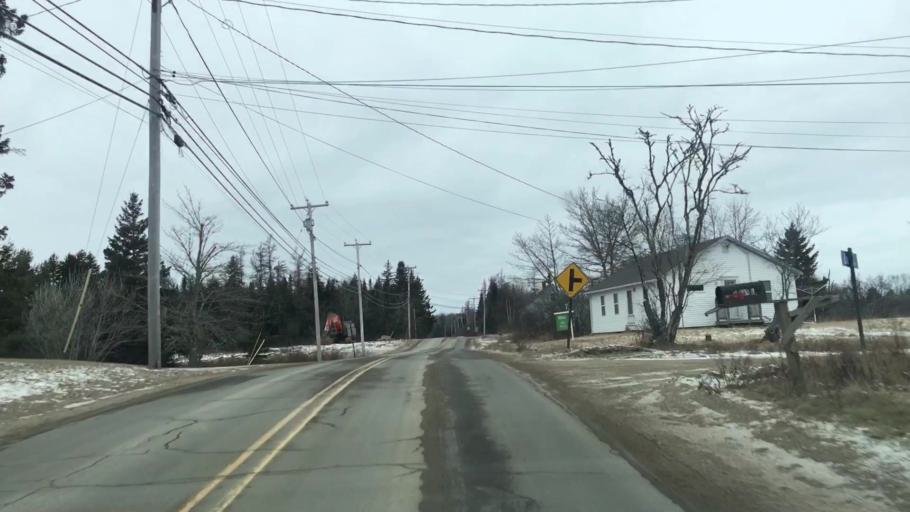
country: US
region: Maine
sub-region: Washington County
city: Machiasport
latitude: 44.7056
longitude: -67.4014
